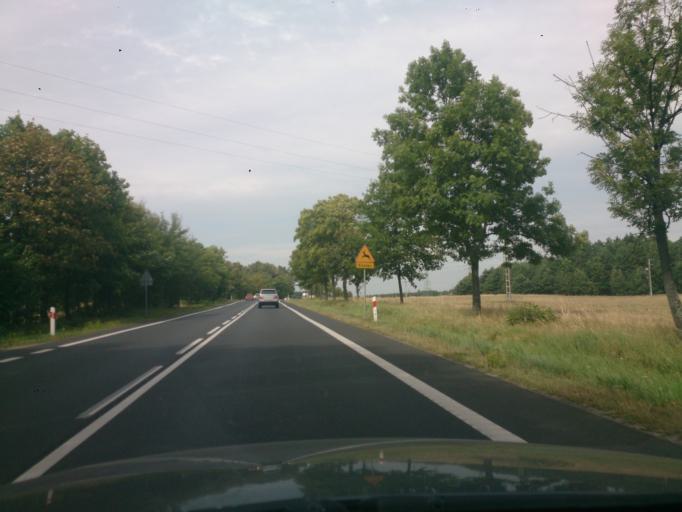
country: PL
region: Subcarpathian Voivodeship
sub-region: Powiat rzeszowski
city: Glogow Malopolski
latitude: 50.1882
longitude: 21.9028
